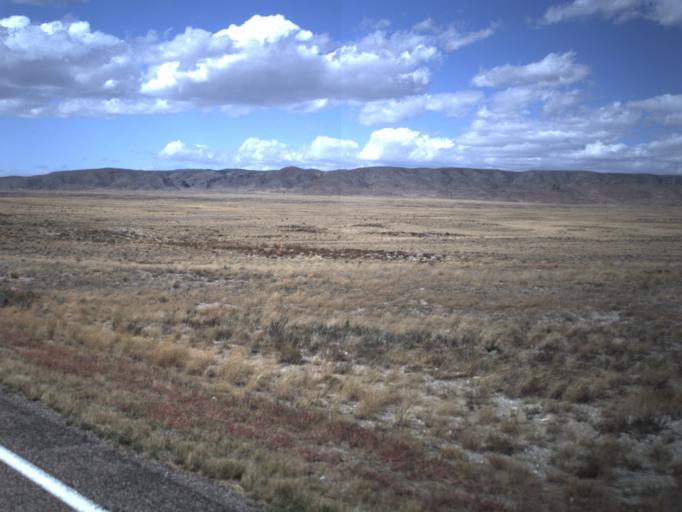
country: US
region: Utah
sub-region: Beaver County
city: Milford
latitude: 38.8022
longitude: -112.8881
